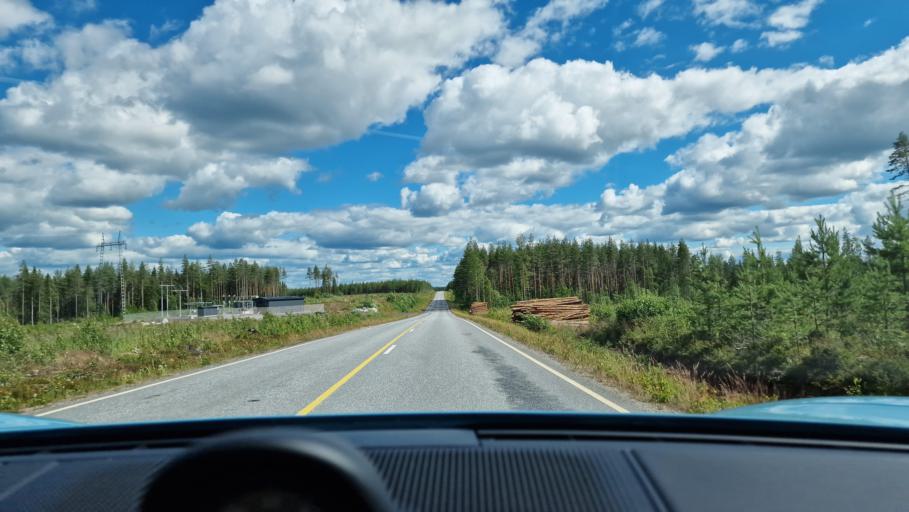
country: FI
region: Central Finland
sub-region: Saarijaervi-Viitasaari
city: Pylkoenmaeki
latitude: 62.6643
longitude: 24.5482
